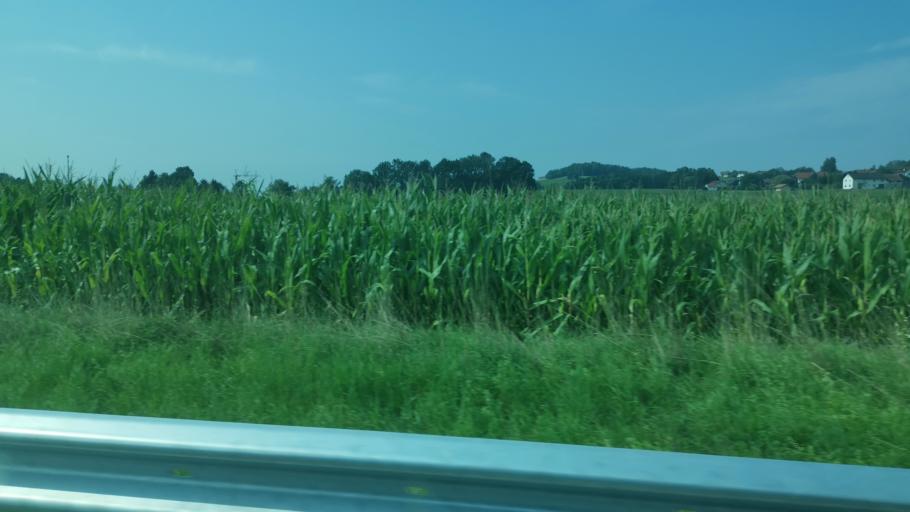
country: DE
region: Bavaria
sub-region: Upper Palatinate
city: Willmering
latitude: 49.2485
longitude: 12.6519
